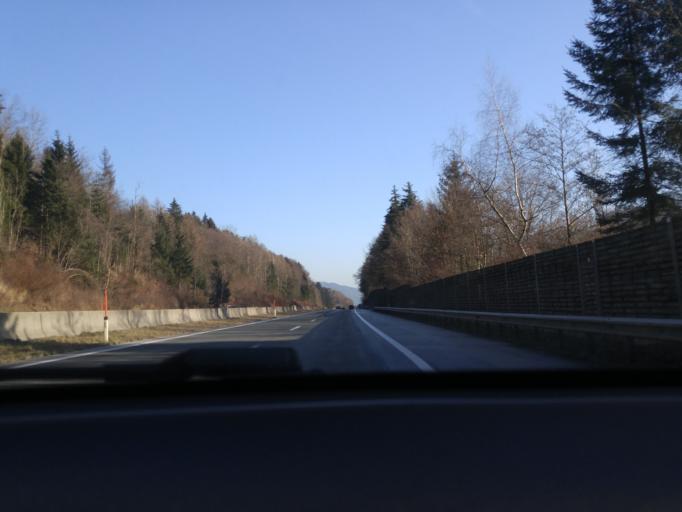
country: AT
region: Salzburg
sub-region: Politischer Bezirk Salzburg-Umgebung
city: Thalgau
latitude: 47.8465
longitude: 13.2523
